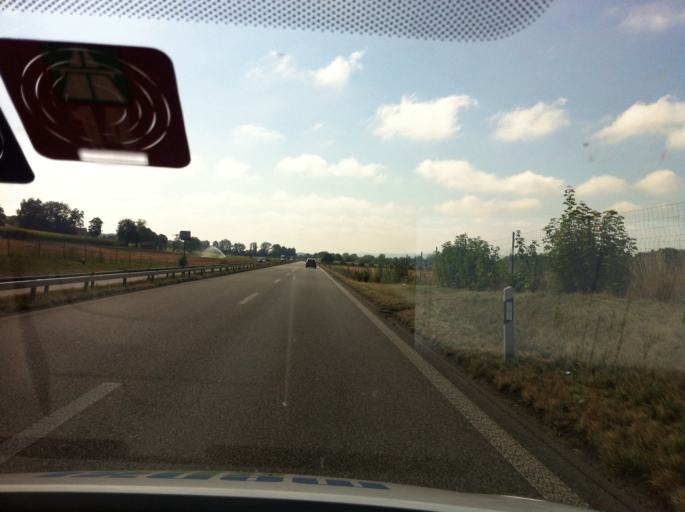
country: CH
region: Zurich
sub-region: Bezirk Buelach
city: Bachenbulach
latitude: 47.4867
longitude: 8.5447
